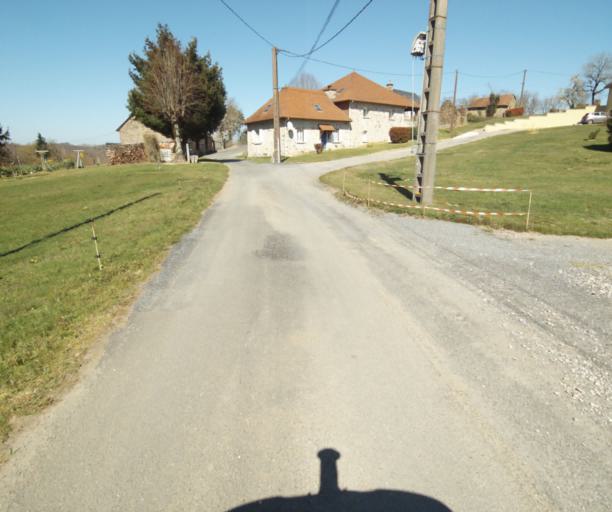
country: FR
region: Limousin
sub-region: Departement de la Correze
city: Chameyrat
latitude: 45.2728
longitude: 1.7114
